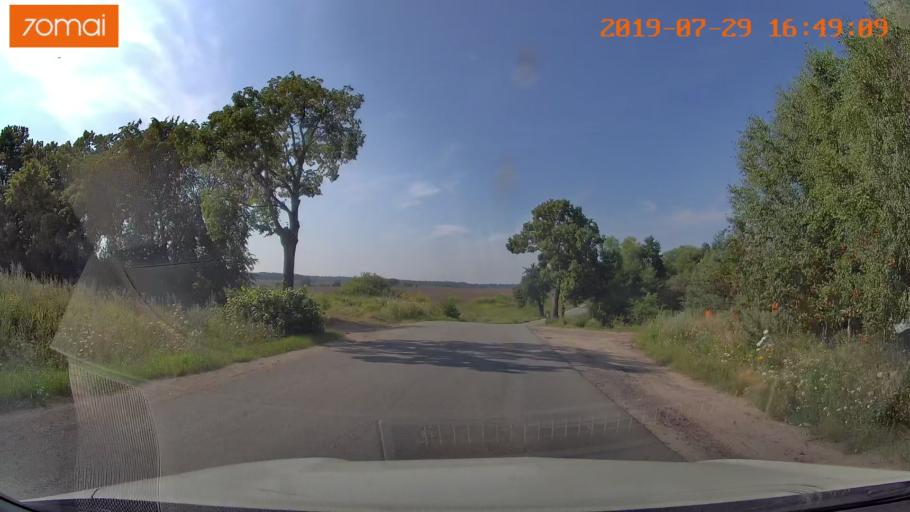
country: RU
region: Kaliningrad
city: Primorsk
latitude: 54.7915
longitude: 20.0680
